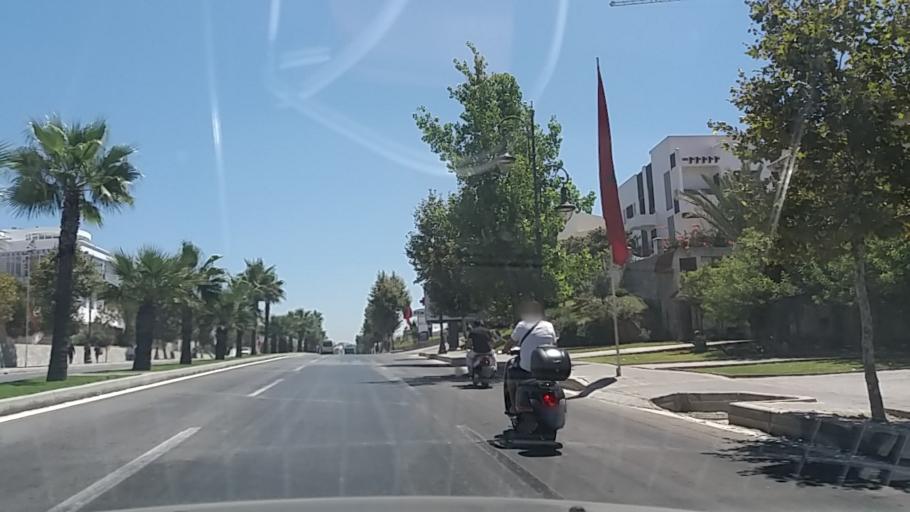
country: MA
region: Tanger-Tetouan
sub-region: Tanger-Assilah
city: Tangier
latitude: 35.7669
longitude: -5.8001
